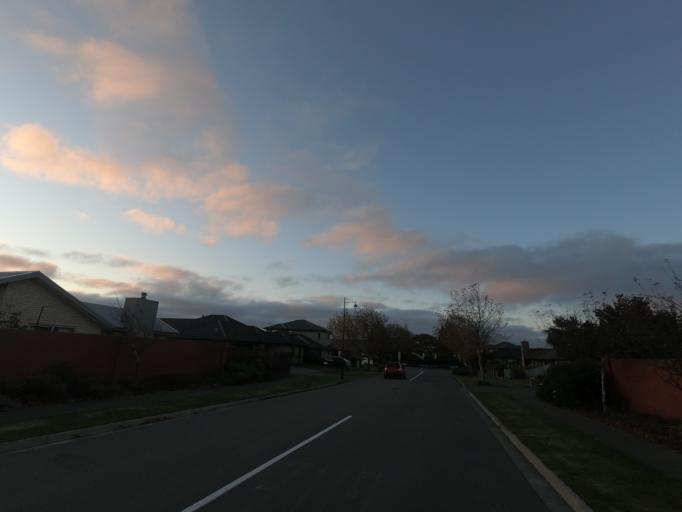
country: NZ
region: Canterbury
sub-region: Selwyn District
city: Prebbleton
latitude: -43.5708
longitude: 172.5692
